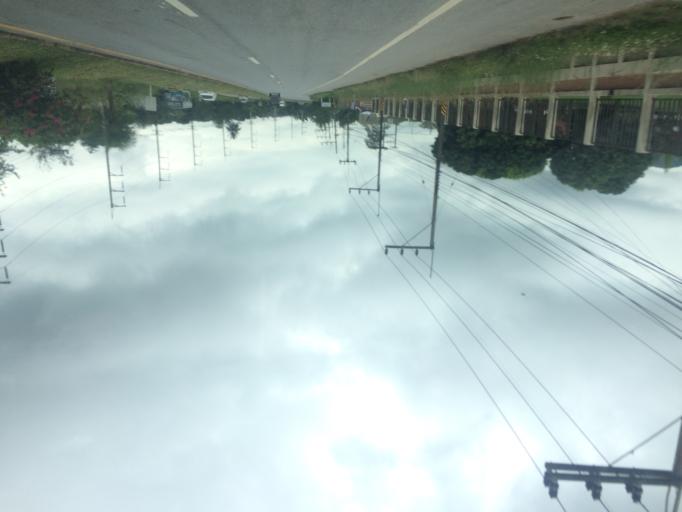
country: TH
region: Chiang Rai
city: Mae Chan
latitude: 20.0887
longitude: 99.8748
